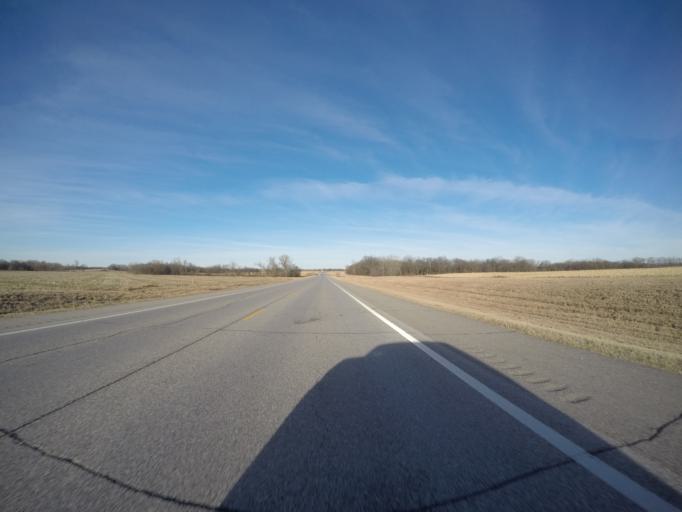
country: US
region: Kansas
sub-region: Marion County
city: Peabody
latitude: 38.1685
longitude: -97.1975
